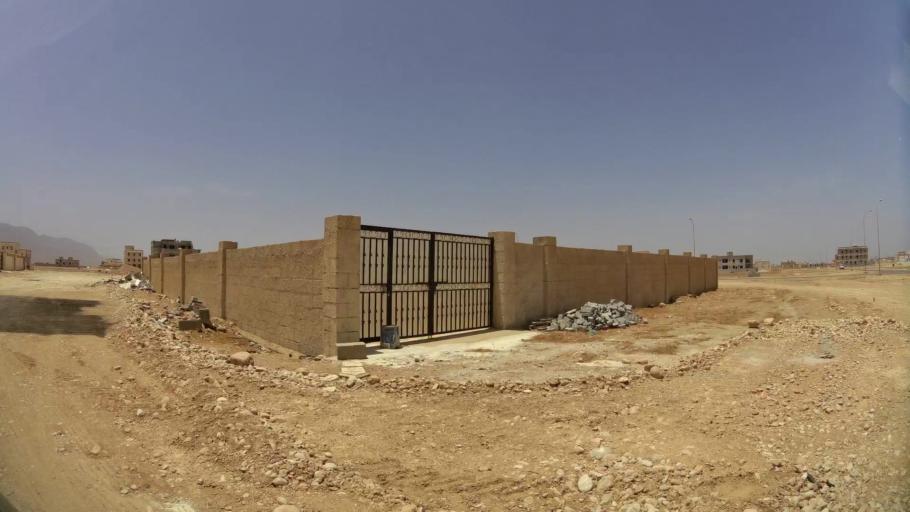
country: OM
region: Zufar
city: Salalah
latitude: 17.0957
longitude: 54.2110
